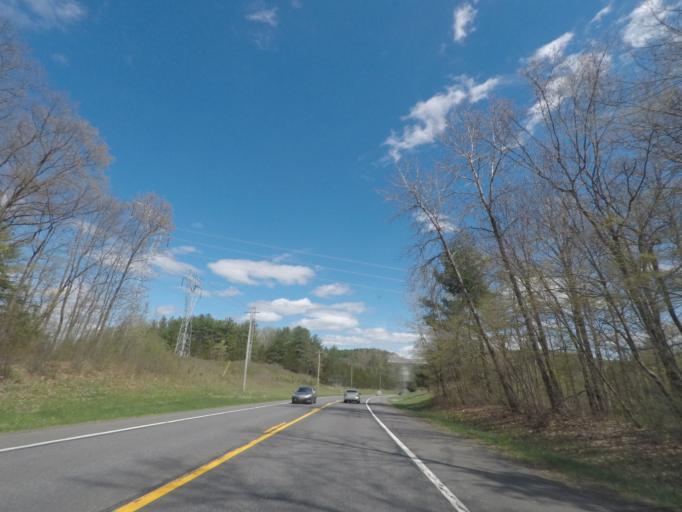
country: US
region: New York
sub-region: Columbia County
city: Hudson
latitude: 42.2187
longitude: -73.8053
